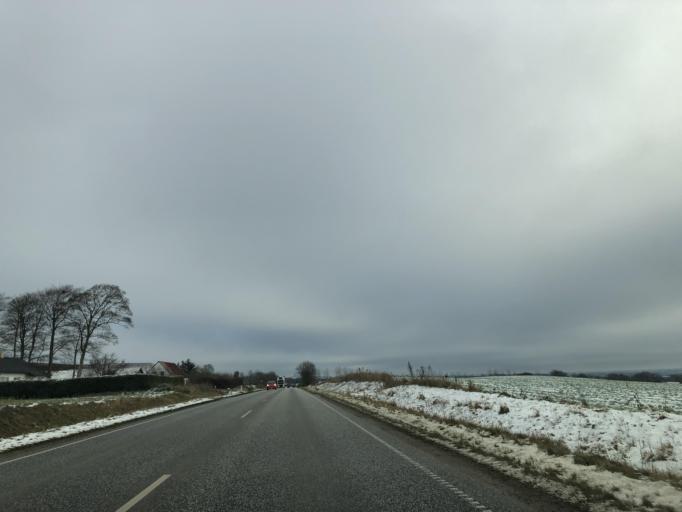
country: DK
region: Central Jutland
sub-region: Horsens Kommune
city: Braedstrup
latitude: 55.8925
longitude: 9.6721
